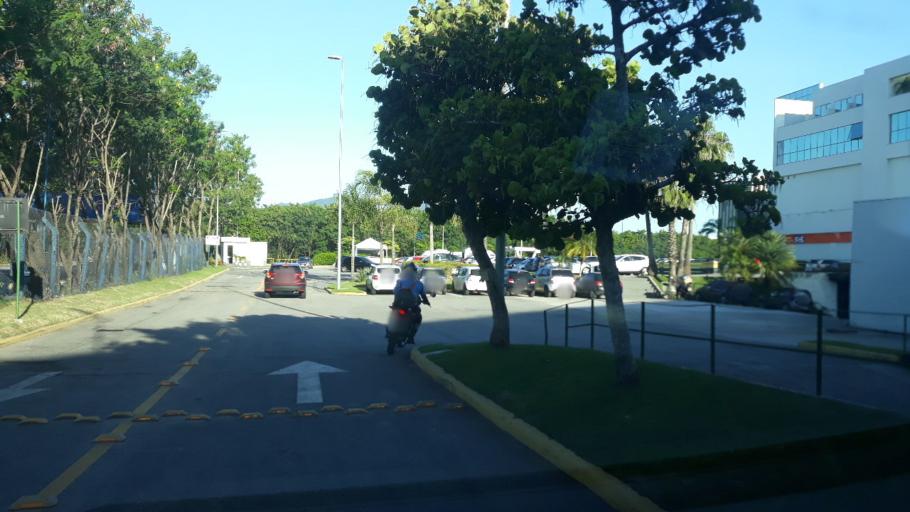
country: BR
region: Rio de Janeiro
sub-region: Rio De Janeiro
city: Rio de Janeiro
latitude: -22.9819
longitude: -43.3623
